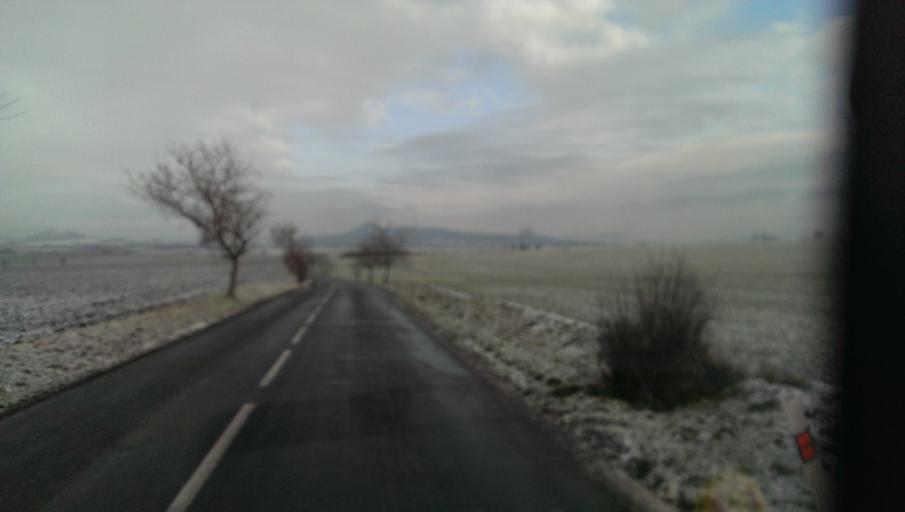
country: CZ
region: Ustecky
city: Trebenice
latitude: 50.4431
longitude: 14.0005
